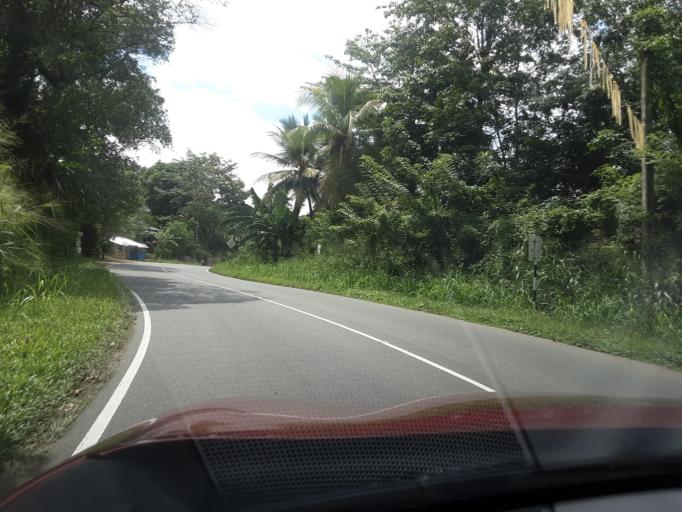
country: LK
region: Uva
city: Monaragala
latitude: 6.8975
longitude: 81.2828
